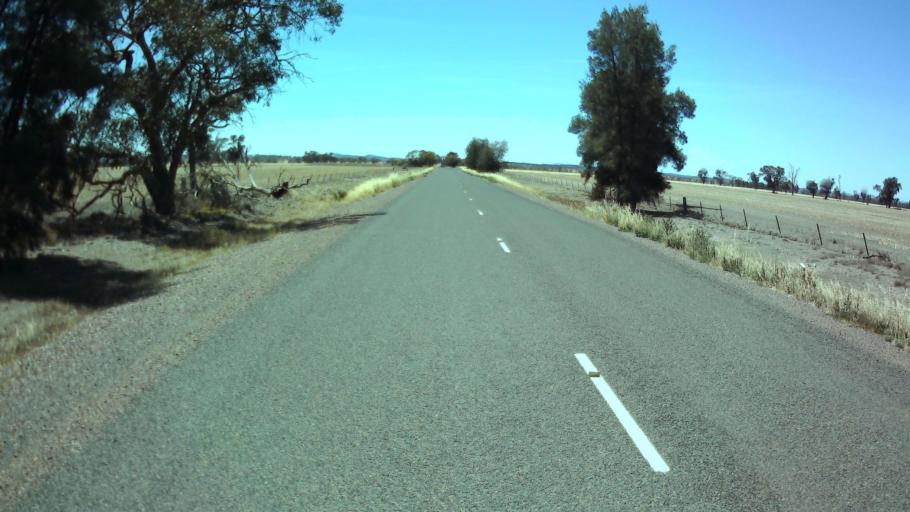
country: AU
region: New South Wales
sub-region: Bland
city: West Wyalong
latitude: -33.6602
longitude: 147.6001
